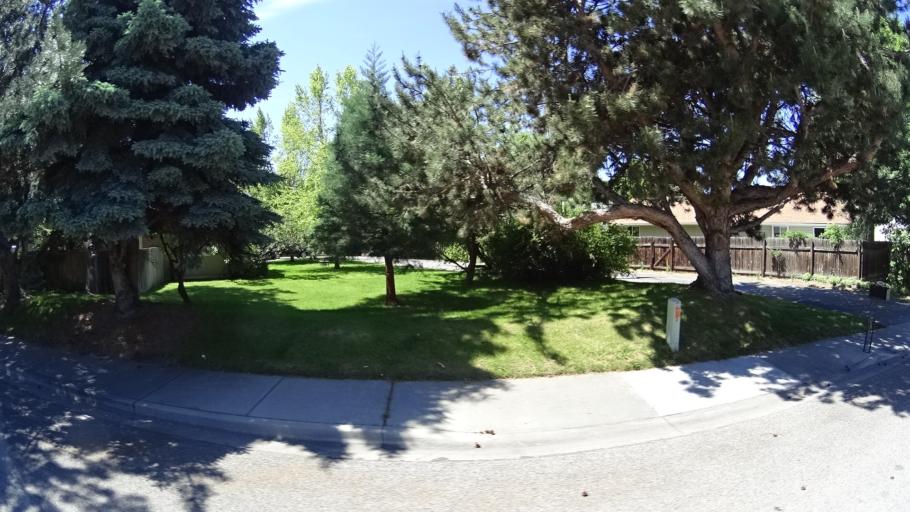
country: US
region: Idaho
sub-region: Ada County
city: Boise
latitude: 43.5671
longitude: -116.1478
